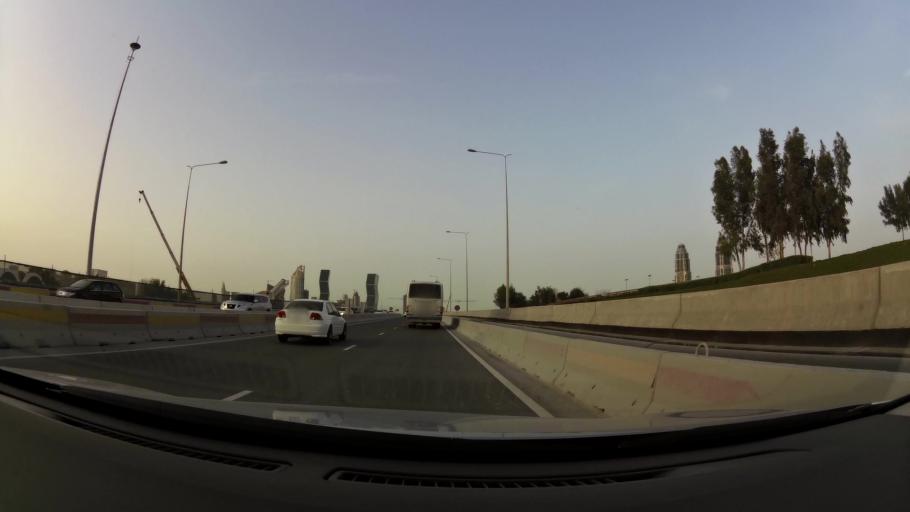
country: QA
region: Baladiyat ad Dawhah
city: Doha
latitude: 25.3664
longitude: 51.5228
